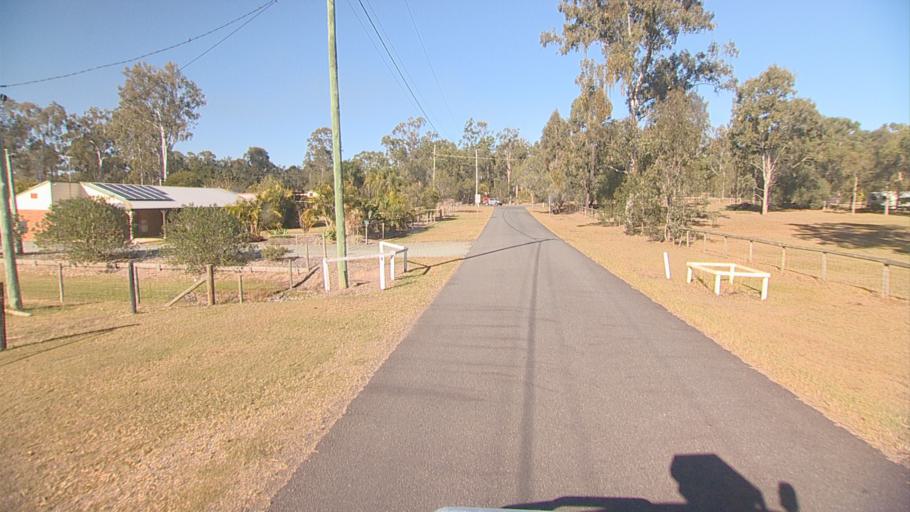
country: AU
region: Queensland
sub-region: Logan
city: North Maclean
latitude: -27.8092
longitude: 152.9885
